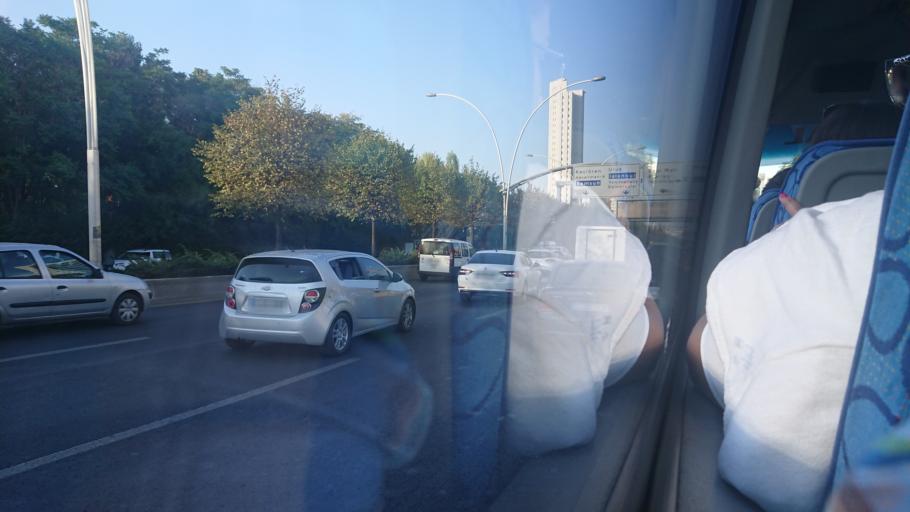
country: TR
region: Ankara
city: Ankara
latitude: 39.9347
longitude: 32.8221
